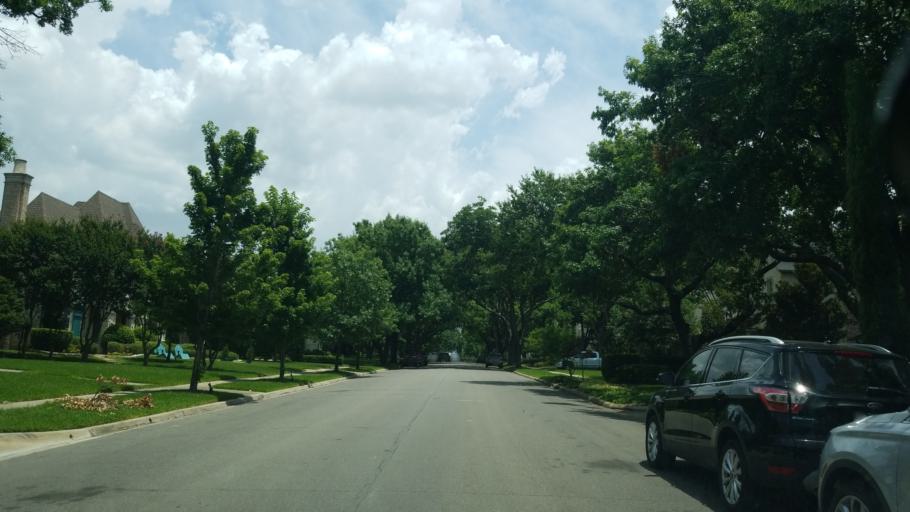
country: US
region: Texas
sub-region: Dallas County
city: University Park
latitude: 32.8706
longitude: -96.7901
